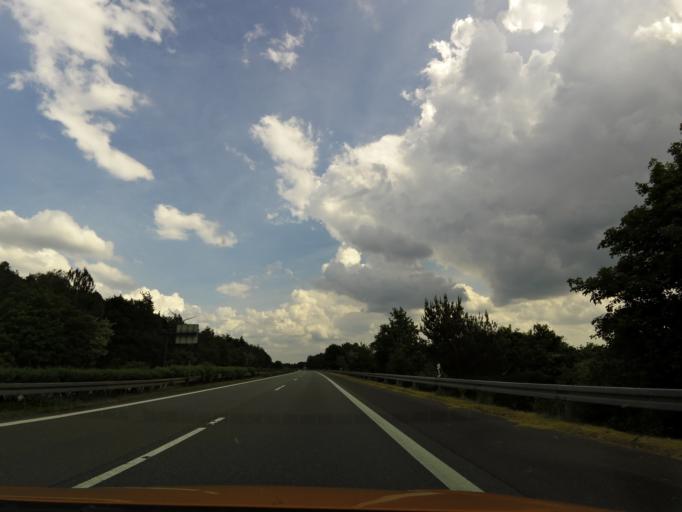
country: DE
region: Brandenburg
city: Heiligengrabe
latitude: 53.1431
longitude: 12.4179
